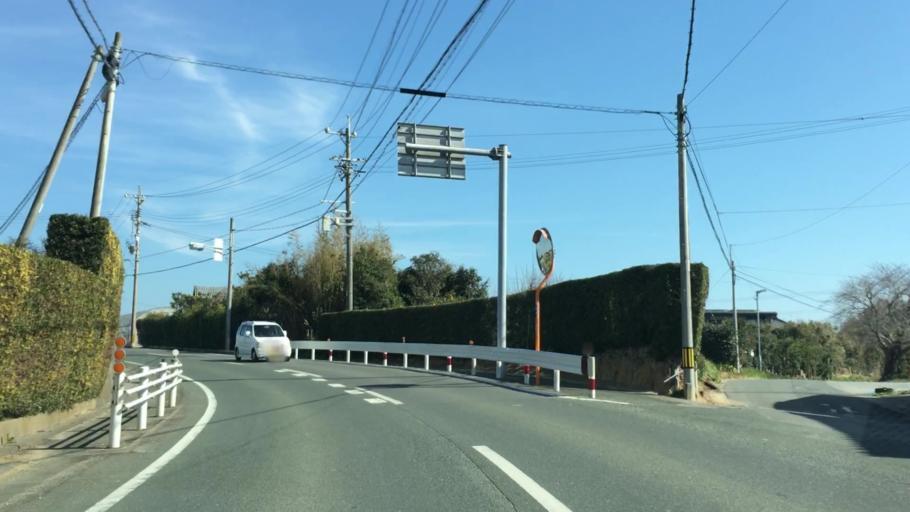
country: JP
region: Aichi
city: Tahara
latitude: 34.6578
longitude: 137.2836
